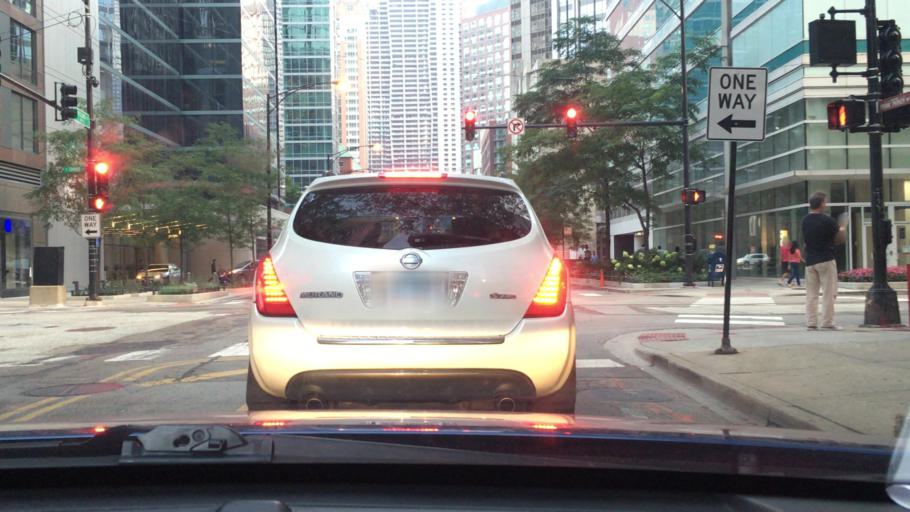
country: US
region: Illinois
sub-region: Cook County
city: Chicago
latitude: 41.8928
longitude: -87.6177
